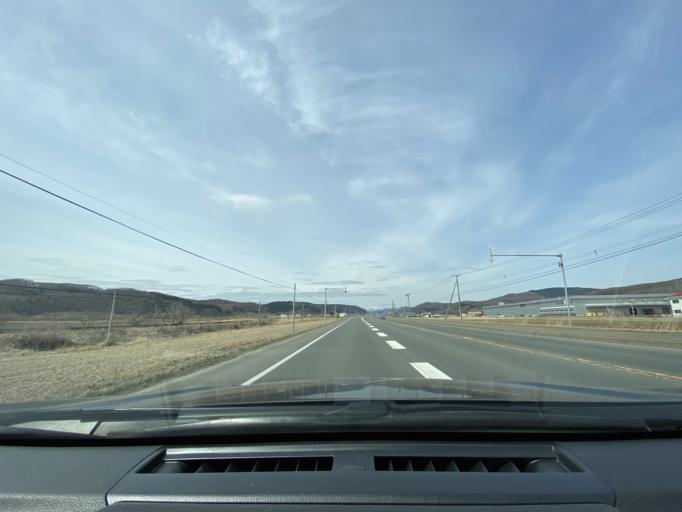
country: JP
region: Hokkaido
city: Kitami
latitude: 43.7921
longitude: 143.7111
